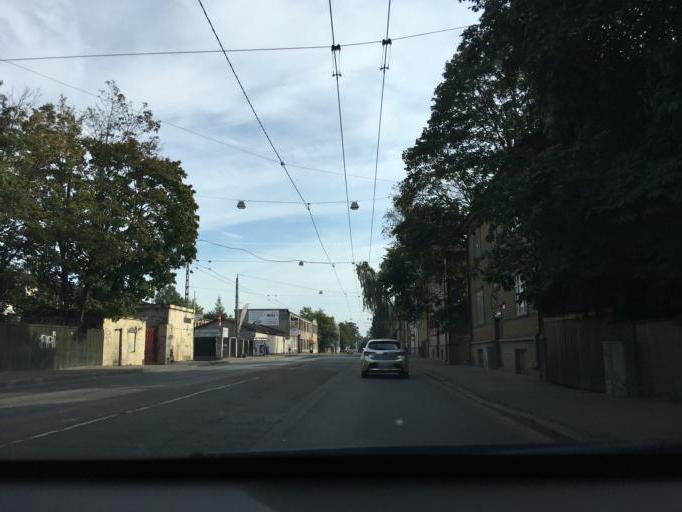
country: EE
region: Harju
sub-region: Tallinna linn
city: Tallinn
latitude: 59.4315
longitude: 24.7176
